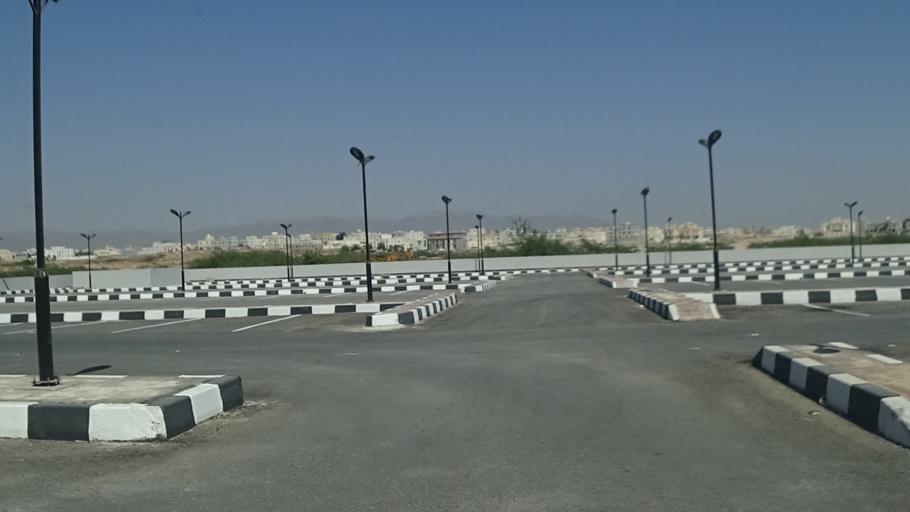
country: OM
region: Zufar
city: Salalah
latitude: 17.0525
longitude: 54.1684
